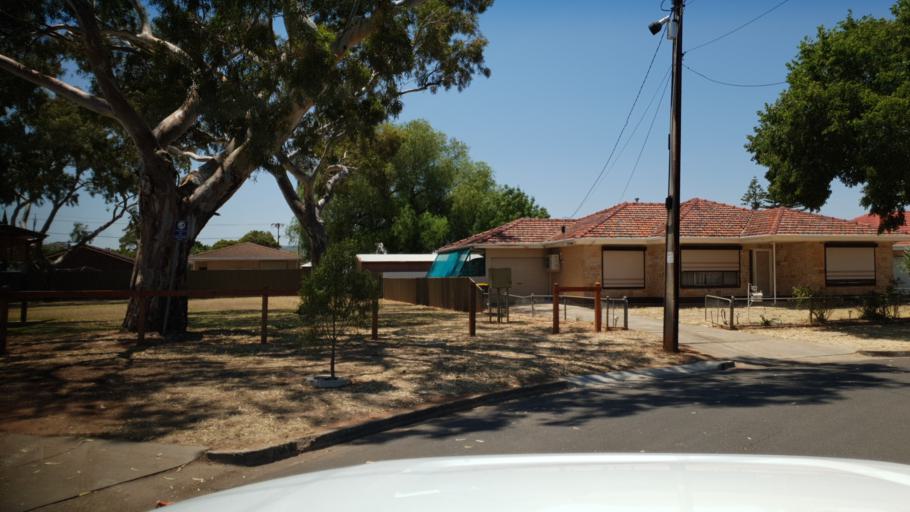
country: AU
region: South Australia
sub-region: Mitcham
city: Clarence Gardens
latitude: -34.9786
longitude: 138.5814
